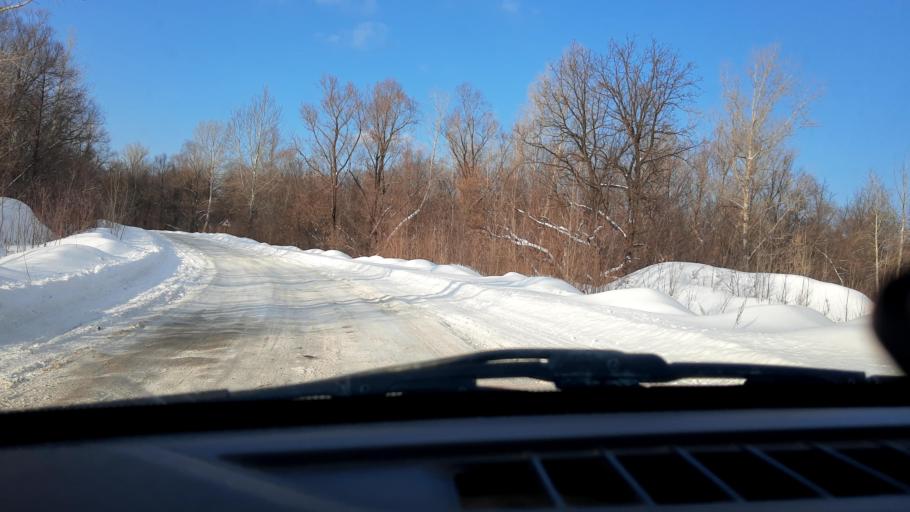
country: RU
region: Bashkortostan
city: Ufa
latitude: 54.6377
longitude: 56.0063
